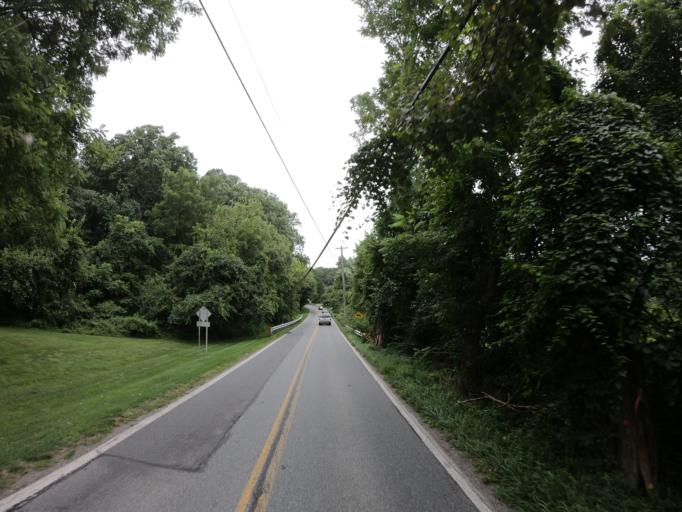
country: US
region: Maryland
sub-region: Montgomery County
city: Montgomery Village
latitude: 39.2082
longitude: -77.2301
